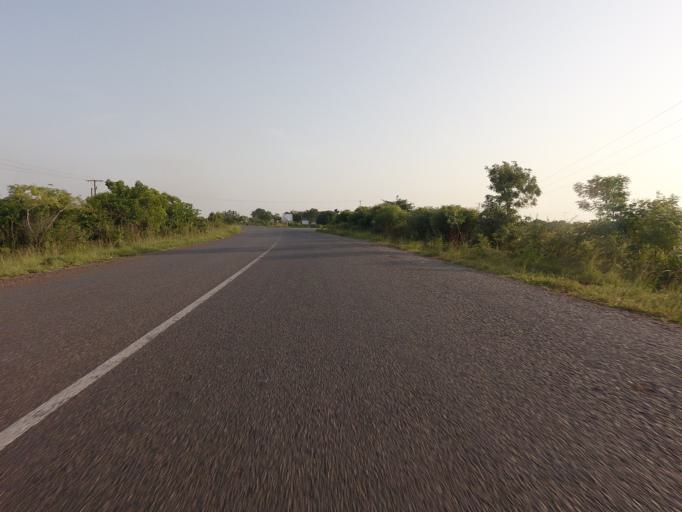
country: GH
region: Volta
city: Anloga
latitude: 5.9696
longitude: 0.6625
